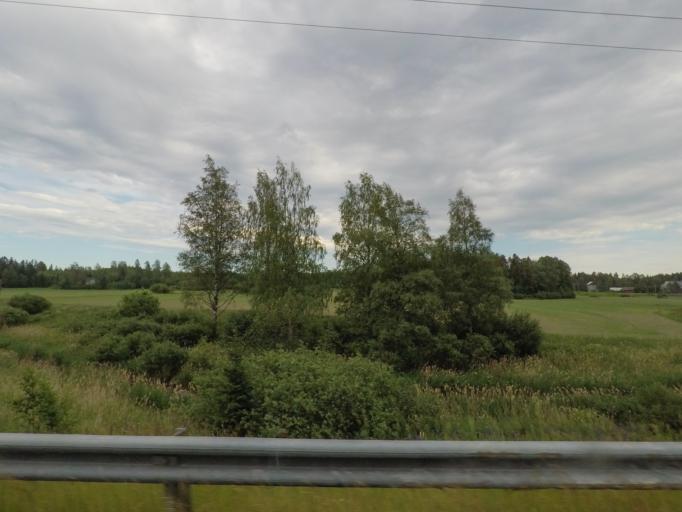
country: FI
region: Uusimaa
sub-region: Helsinki
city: Maentsaelae
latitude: 60.6889
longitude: 25.3735
